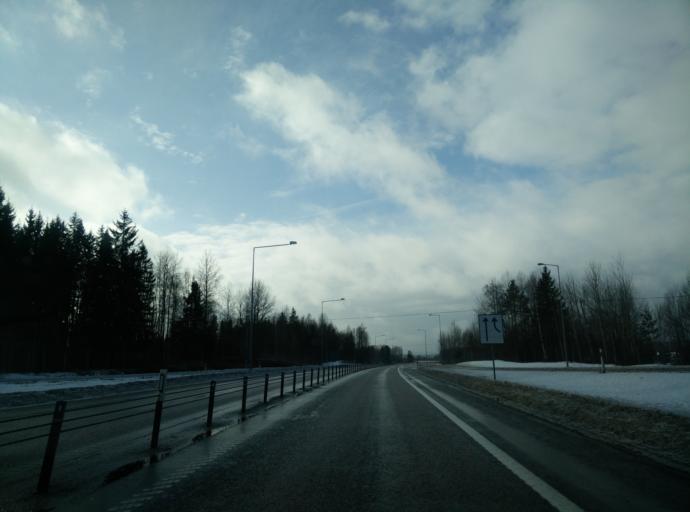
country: SE
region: Gaevleborg
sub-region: Sandvikens Kommun
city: Jarbo
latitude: 60.6020
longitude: 16.5862
